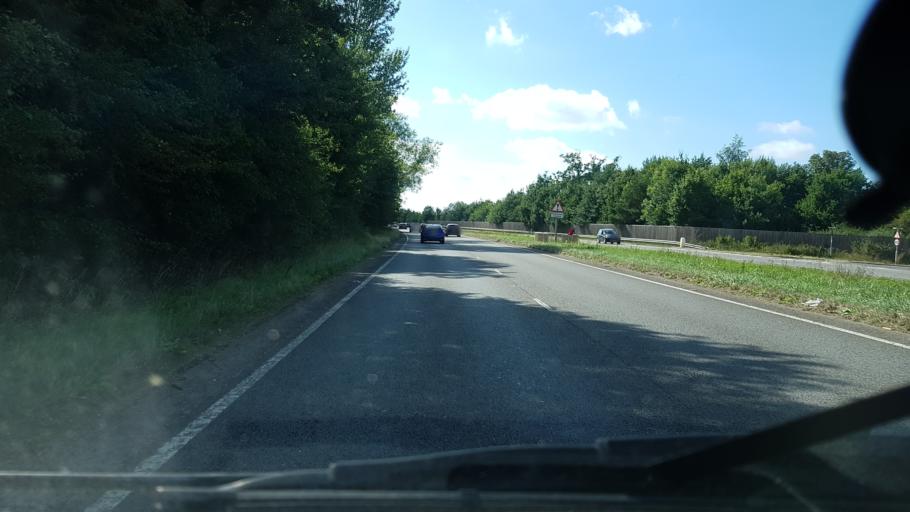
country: GB
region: England
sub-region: West Sussex
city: Horsham
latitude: 51.0890
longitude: -0.3197
